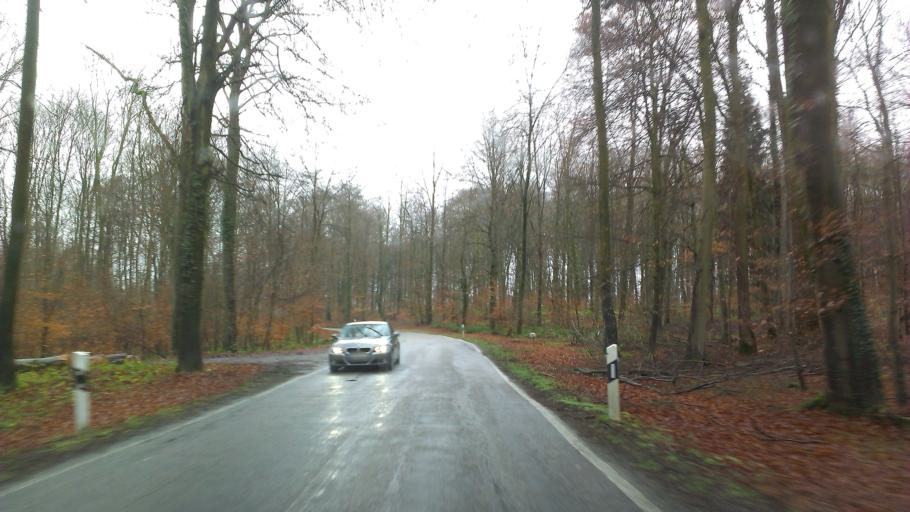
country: DE
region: Baden-Wuerttemberg
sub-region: Karlsruhe Region
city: Gondelsheim
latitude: 49.0991
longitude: 8.6879
